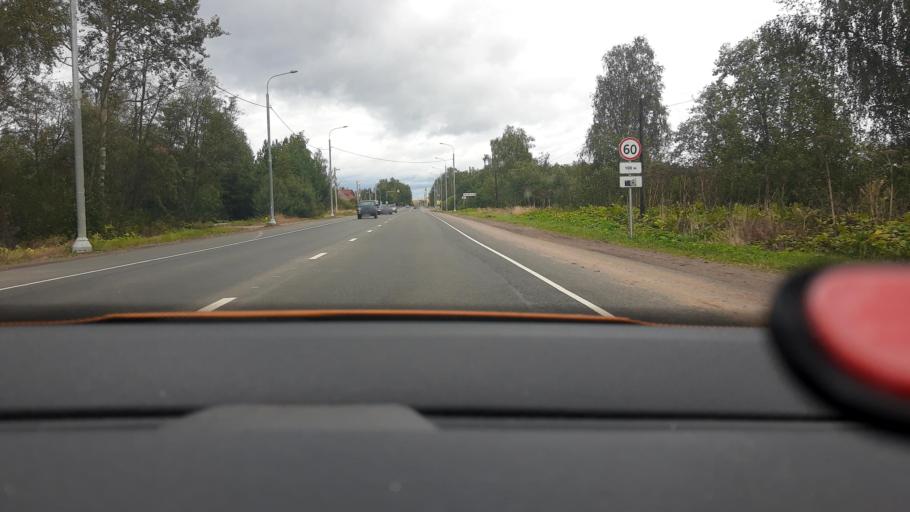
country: RU
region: Moskovskaya
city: Krasnoarmeysk
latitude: 56.0720
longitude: 38.0335
